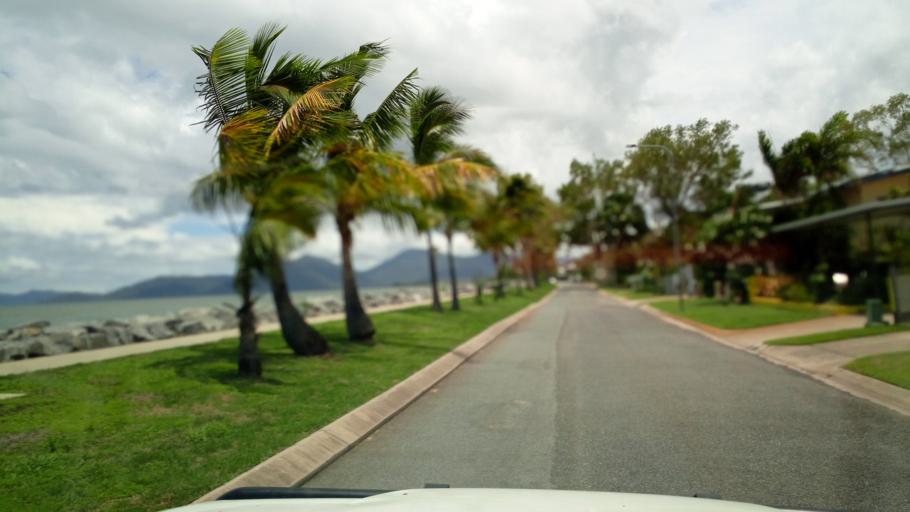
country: AU
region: Queensland
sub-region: Cairns
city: Yorkeys Knob
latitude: -16.8491
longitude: 145.7480
